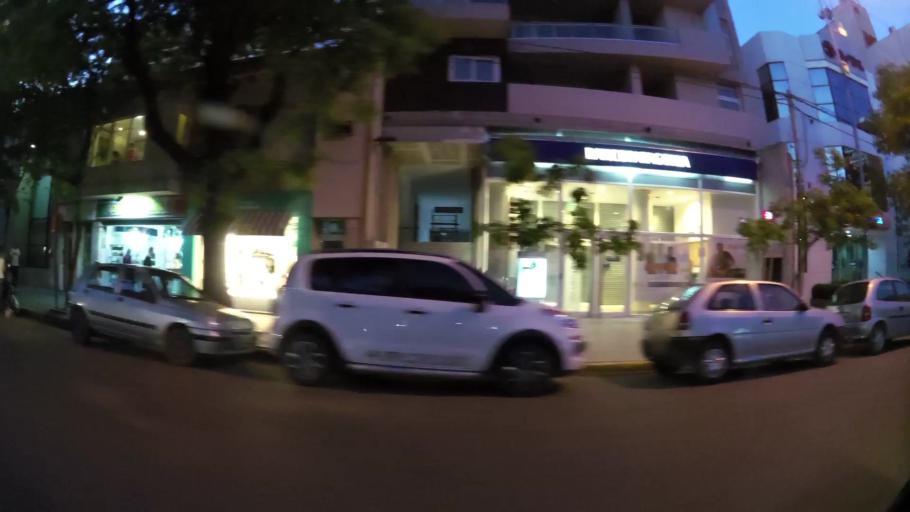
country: AR
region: Cordoba
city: Villa Maria
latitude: -32.4099
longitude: -63.2440
